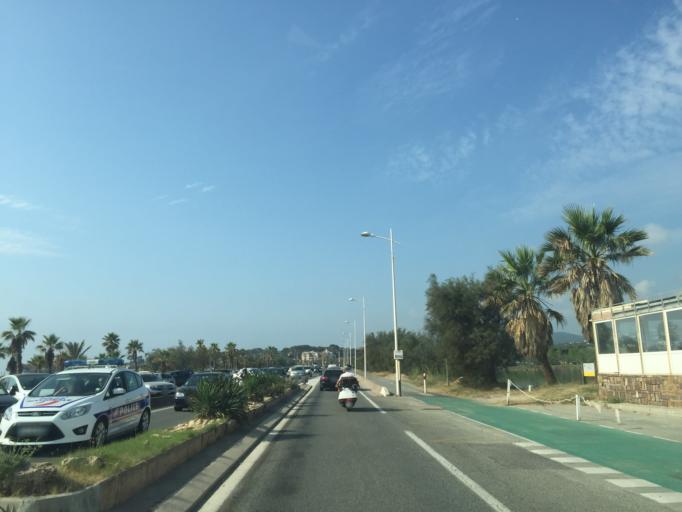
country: FR
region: Provence-Alpes-Cote d'Azur
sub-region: Departement du Var
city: Frejus
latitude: 43.3984
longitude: 6.7295
